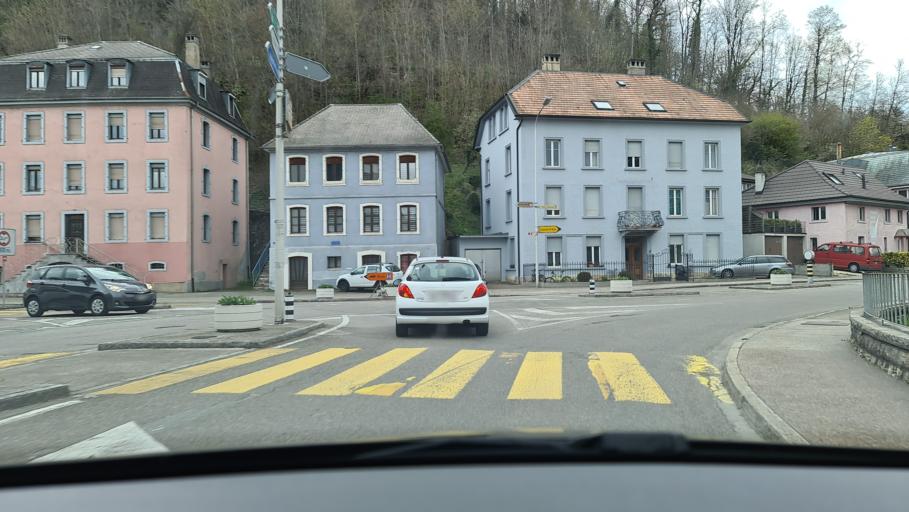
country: CH
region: Jura
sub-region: Porrentruy District
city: Porrentruy
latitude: 47.4217
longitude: 7.0773
